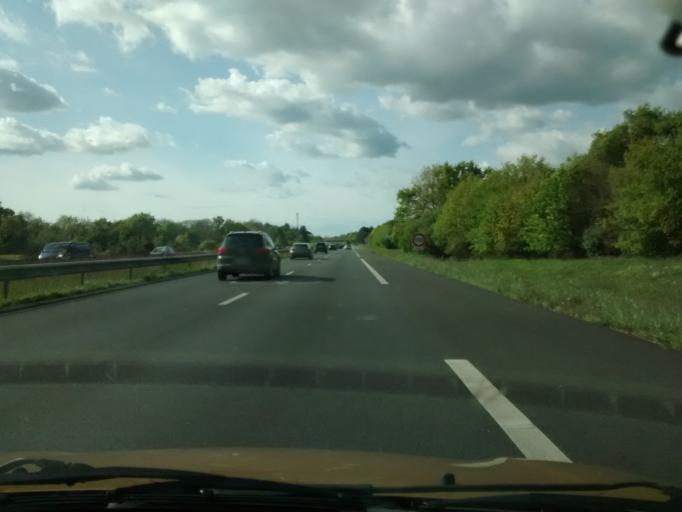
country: FR
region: Pays de la Loire
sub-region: Departement de la Loire-Atlantique
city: Le Temple-de-Bretagne
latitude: 47.3175
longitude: -1.7721
